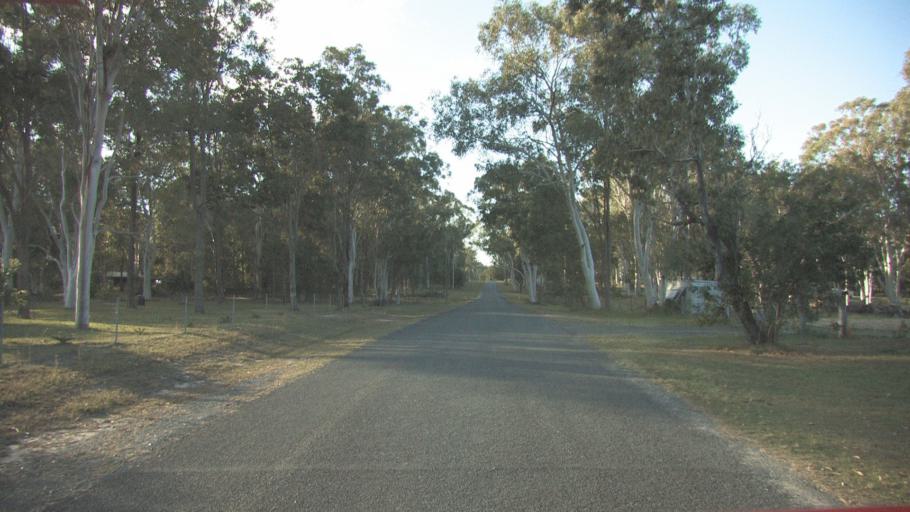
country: AU
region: Queensland
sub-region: Logan
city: Cedar Vale
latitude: -27.8476
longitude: 153.1102
